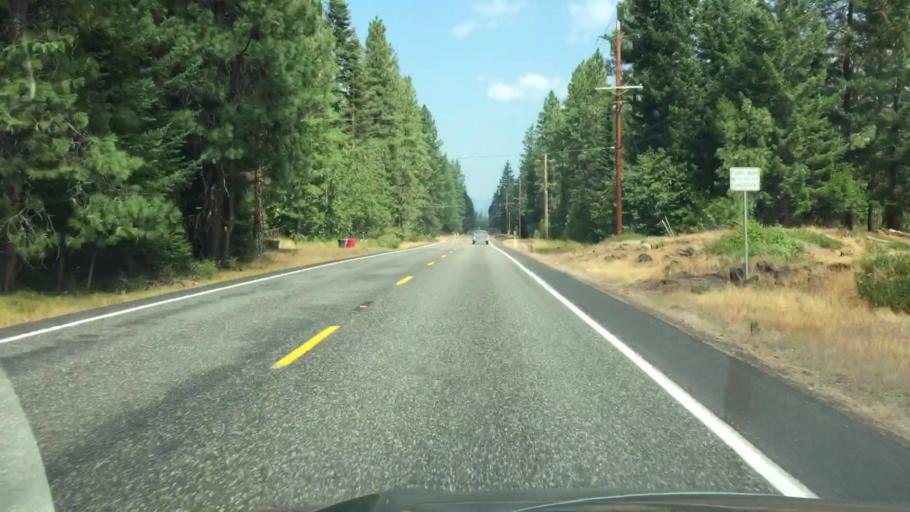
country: US
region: Washington
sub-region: Klickitat County
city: White Salmon
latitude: 45.9309
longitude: -121.4949
